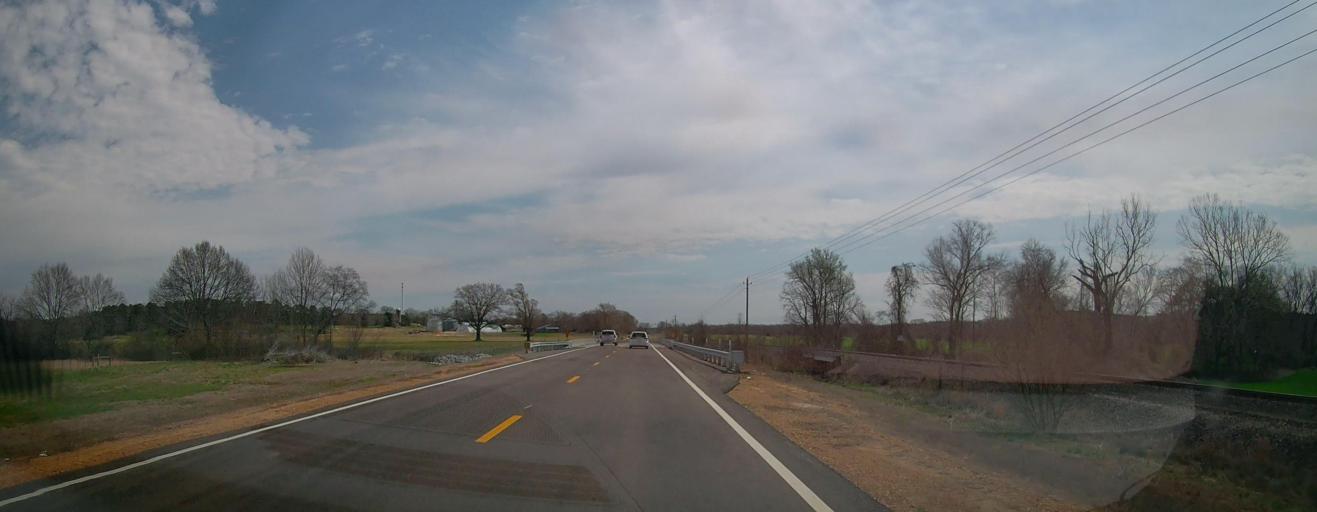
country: US
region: Mississippi
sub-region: Benton County
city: Ashland
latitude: 34.6224
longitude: -89.2386
